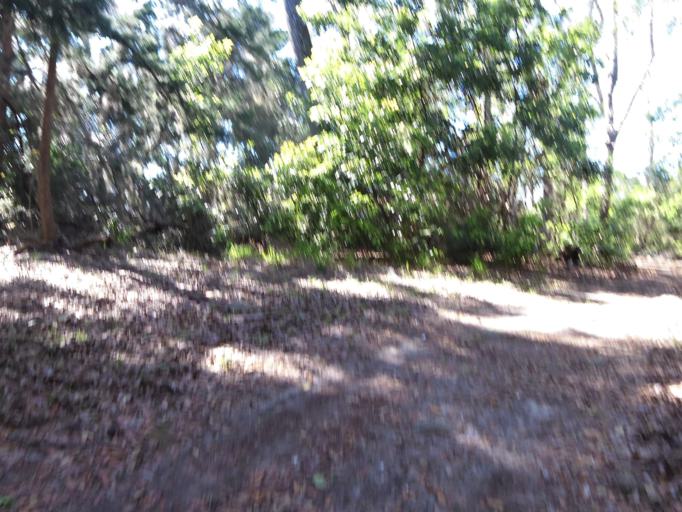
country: US
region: Florida
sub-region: Saint Johns County
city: Villano Beach
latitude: 29.9917
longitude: -81.3285
